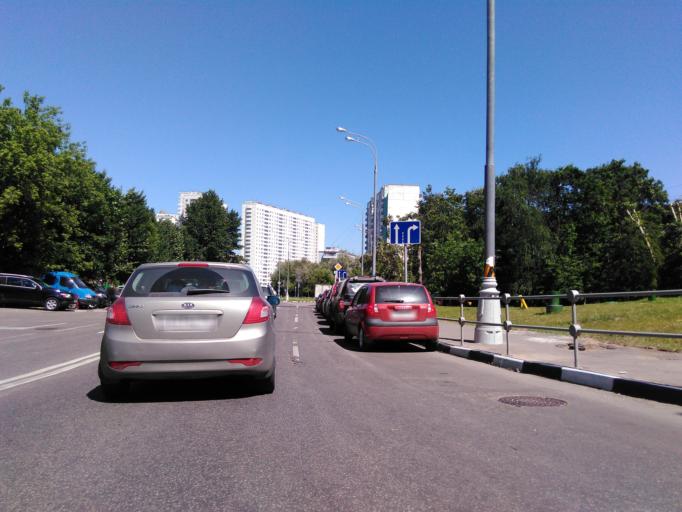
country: RU
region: Moskovskaya
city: Cheremushki
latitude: 55.6596
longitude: 37.5630
